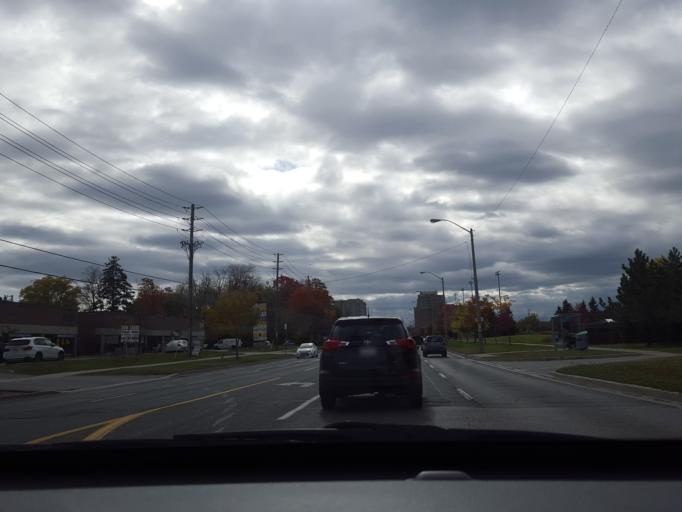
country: CA
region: Ontario
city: Markham
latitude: 43.8178
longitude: -79.3044
